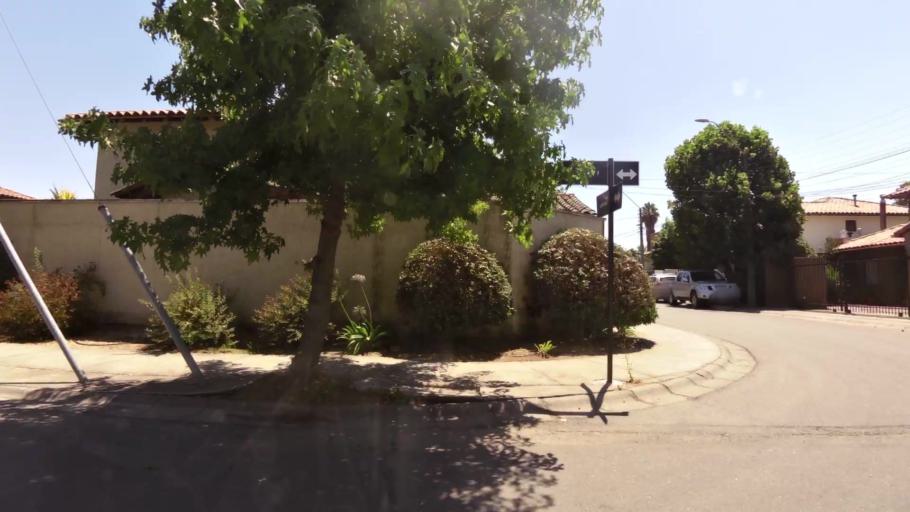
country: CL
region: Maule
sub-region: Provincia de Curico
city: Curico
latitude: -34.9892
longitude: -71.2268
